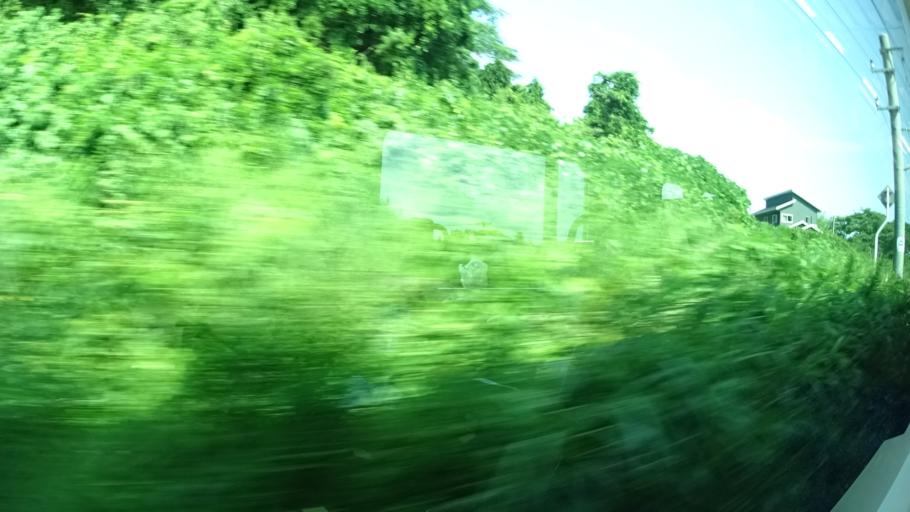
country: JP
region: Miyagi
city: Wakuya
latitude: 38.4905
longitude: 141.0889
